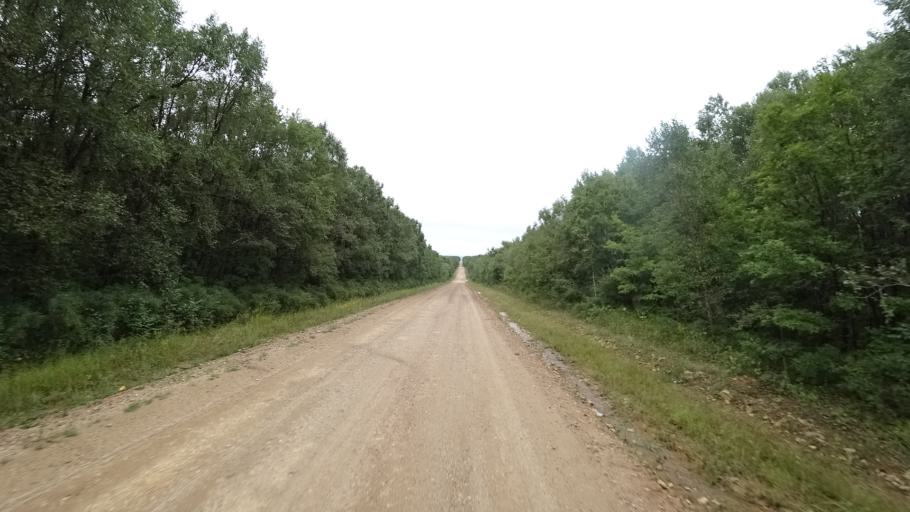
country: RU
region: Primorskiy
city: Ivanovka
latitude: 44.0354
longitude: 132.5342
